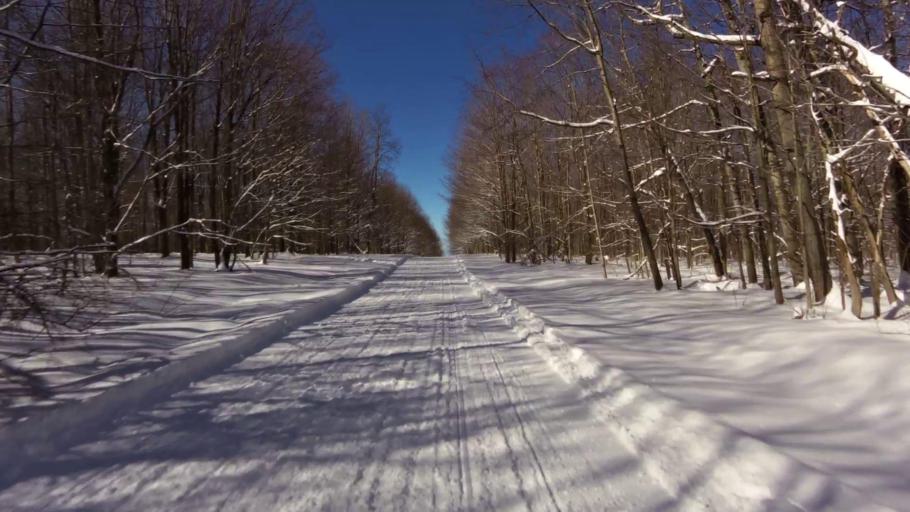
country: US
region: New York
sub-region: Chautauqua County
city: Mayville
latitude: 42.2356
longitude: -79.3845
